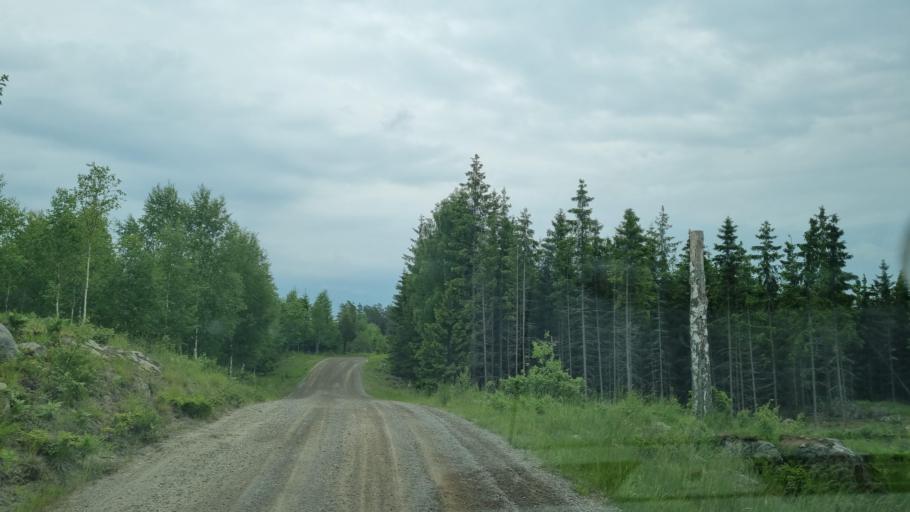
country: SE
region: OEstergoetland
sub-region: Atvidabergs Kommun
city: Atvidaberg
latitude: 58.2585
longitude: 16.0551
